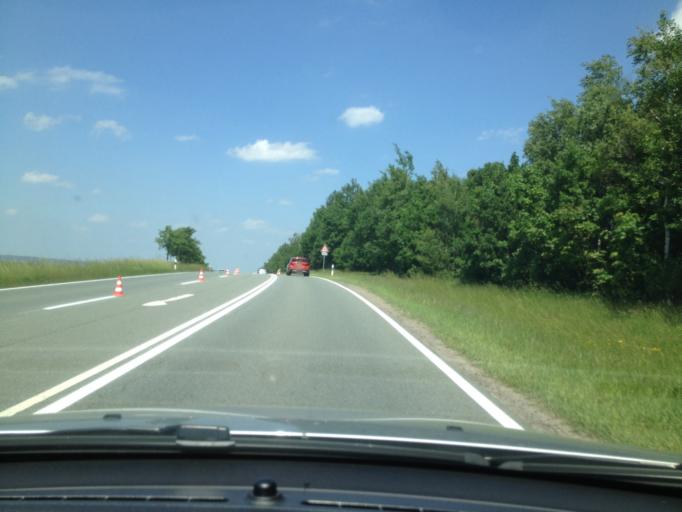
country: DE
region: Saxony
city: Burkhardtsdorf
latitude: 50.7559
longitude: 12.9298
